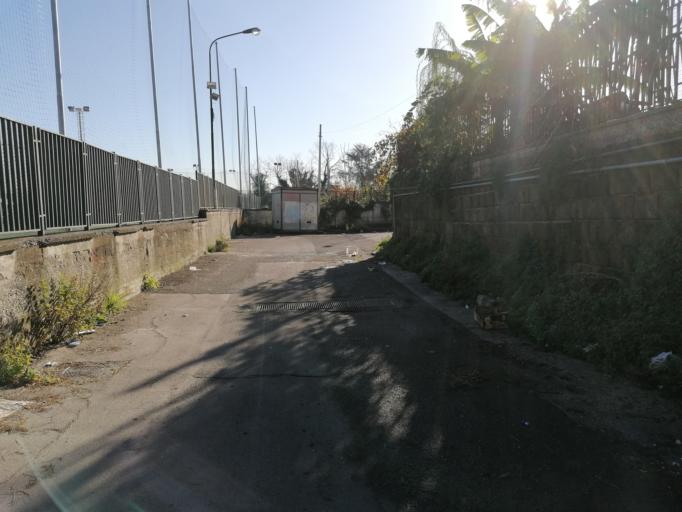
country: IT
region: Campania
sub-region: Provincia di Napoli
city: Casavatore
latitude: 40.8853
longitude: 14.2620
